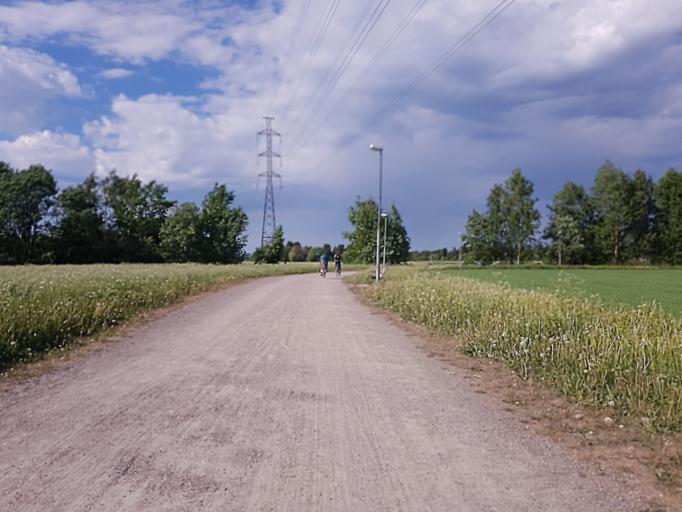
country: FI
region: Uusimaa
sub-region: Helsinki
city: Vantaa
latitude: 60.2462
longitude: 24.9745
